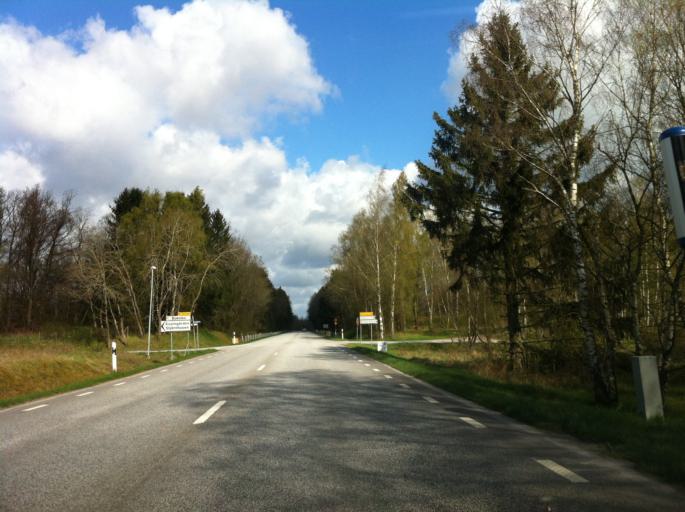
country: SE
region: Skane
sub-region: Hoors Kommun
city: Satofta
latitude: 55.9104
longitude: 13.6024
